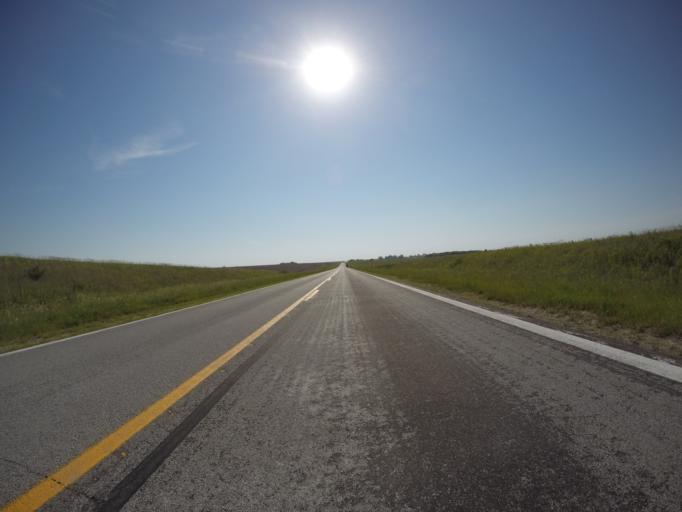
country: US
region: Nebraska
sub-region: Pawnee County
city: Pawnee City
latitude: 40.0447
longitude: -96.3799
